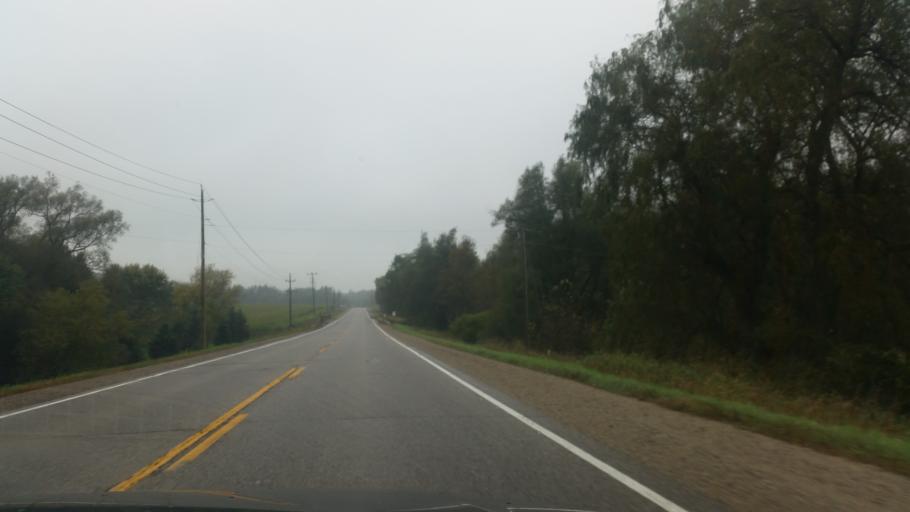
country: CA
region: Ontario
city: Waterloo
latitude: 43.6558
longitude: -80.4962
